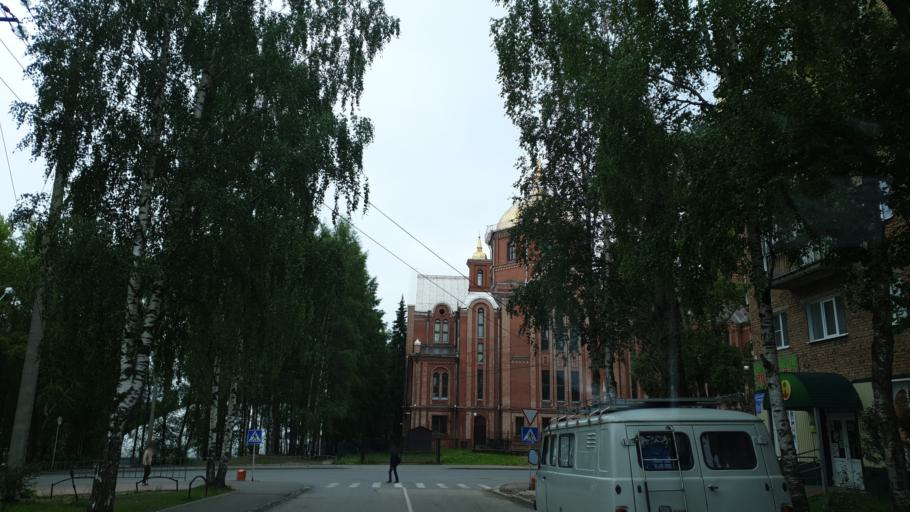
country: RU
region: Komi Republic
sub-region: Syktyvdinskiy Rayon
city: Syktyvkar
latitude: 61.6601
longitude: 50.8231
